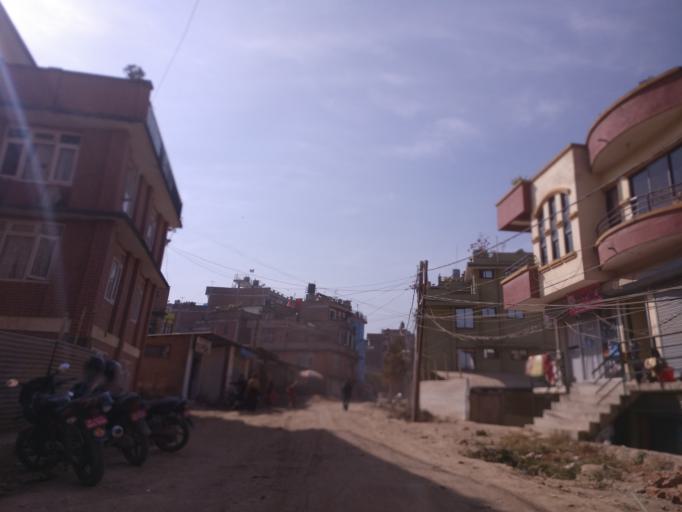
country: NP
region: Central Region
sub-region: Bagmati Zone
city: Patan
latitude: 27.6750
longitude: 85.3304
